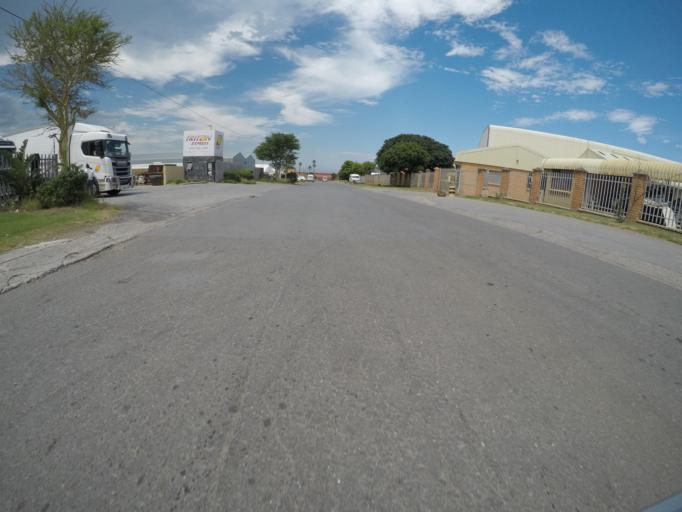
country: ZA
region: Eastern Cape
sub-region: Buffalo City Metropolitan Municipality
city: East London
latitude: -33.0301
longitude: 27.8760
